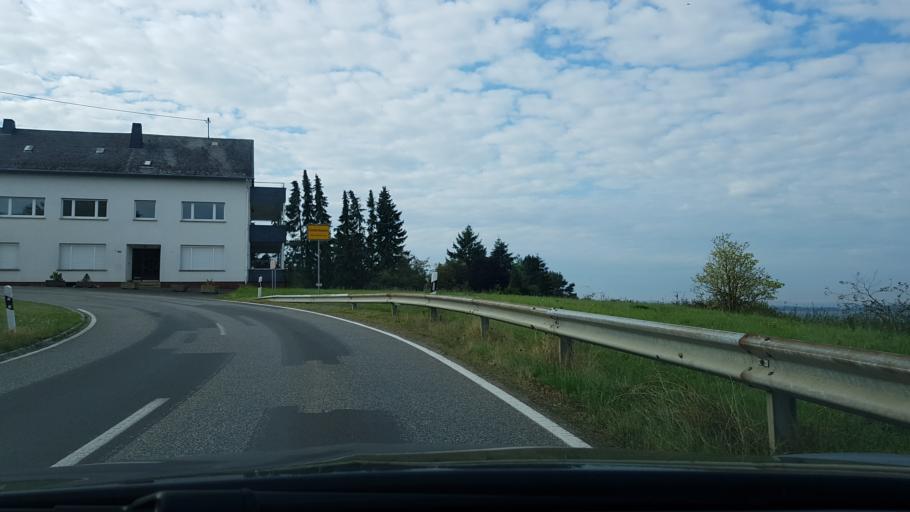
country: DE
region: Rheinland-Pfalz
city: Mermuth
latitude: 50.1593
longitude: 7.4802
